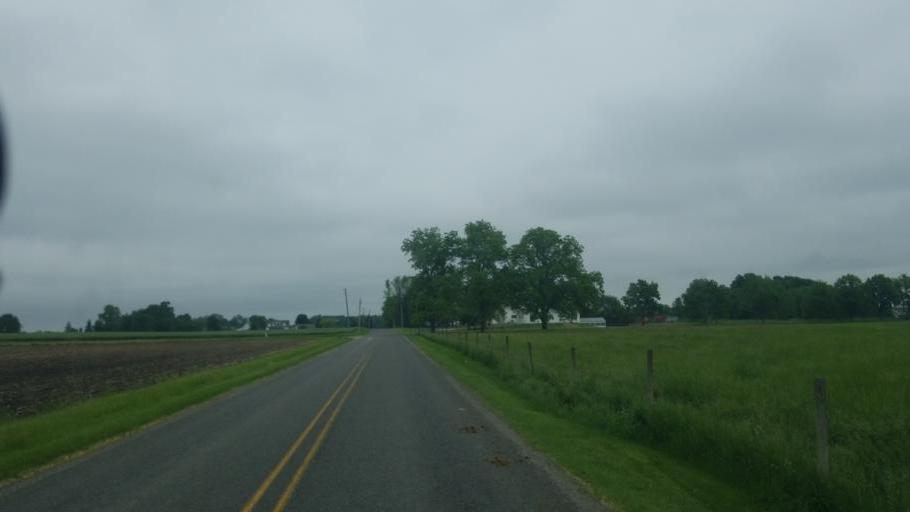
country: US
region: Indiana
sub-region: Elkhart County
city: Nappanee
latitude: 41.4635
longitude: -86.0497
